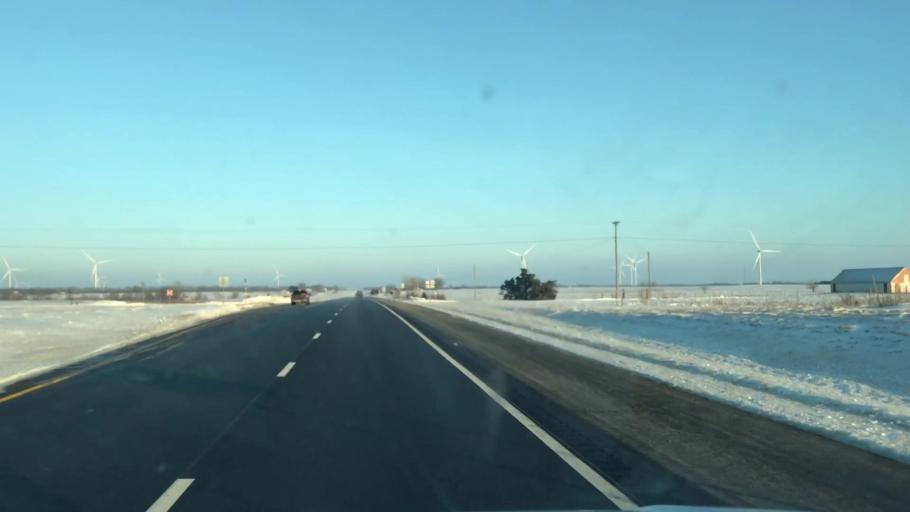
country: US
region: Missouri
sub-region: DeKalb County
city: Maysville
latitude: 39.7617
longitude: -94.4340
